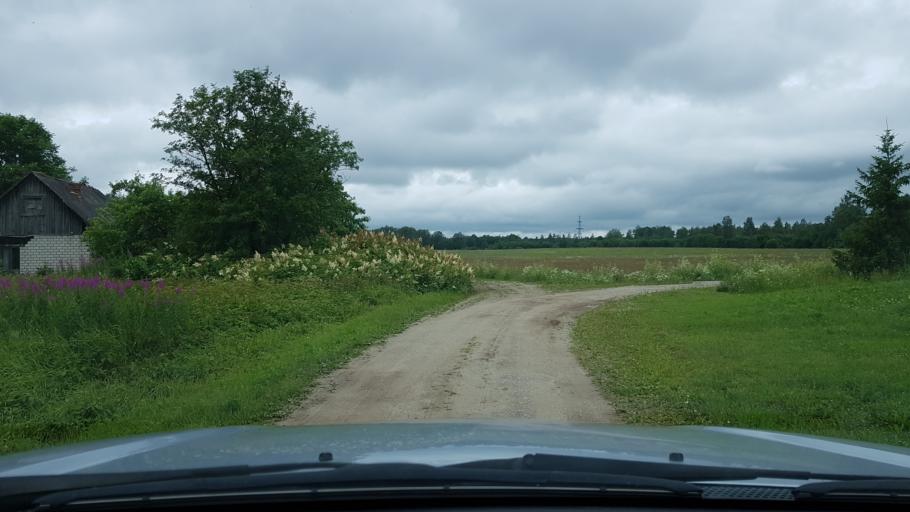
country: EE
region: Ida-Virumaa
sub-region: Narva-Joesuu linn
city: Narva-Joesuu
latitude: 59.3483
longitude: 28.0186
